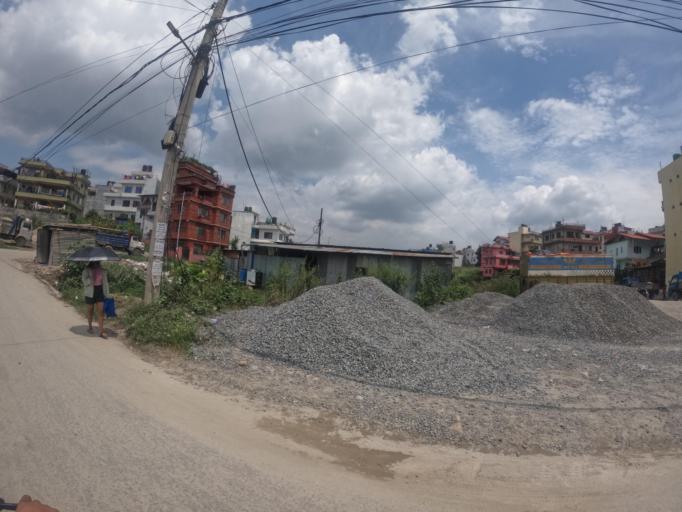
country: NP
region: Central Region
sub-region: Bagmati Zone
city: Kathmandu
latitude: 27.6777
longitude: 85.3657
